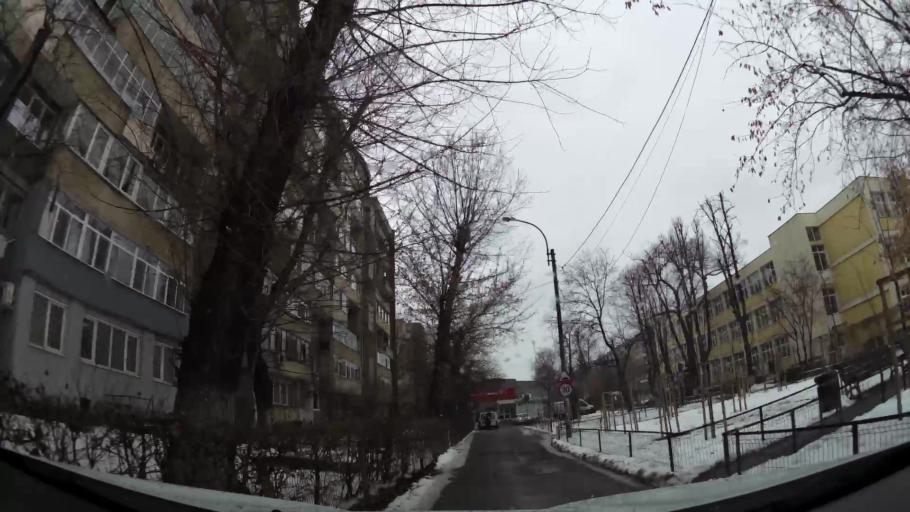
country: RO
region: Ilfov
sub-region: Comuna Chiajna
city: Rosu
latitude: 44.4238
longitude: 26.0387
